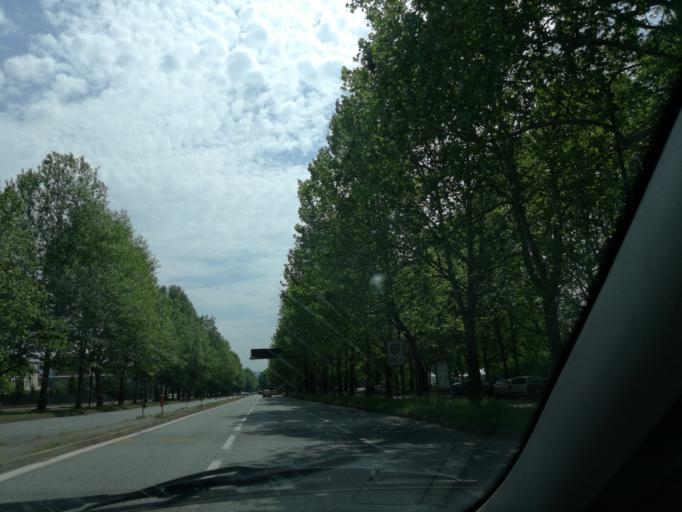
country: IT
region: Piedmont
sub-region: Provincia di Torino
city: Savonera
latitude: 45.0891
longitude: 7.6460
